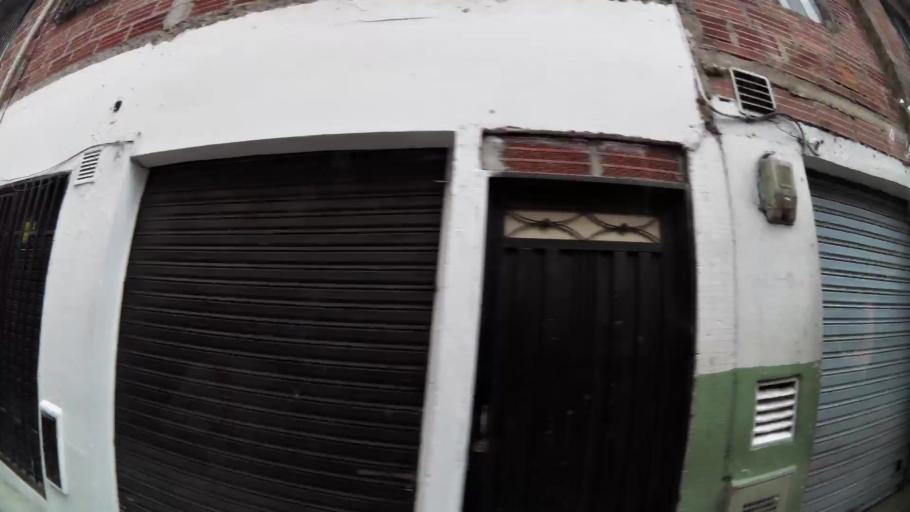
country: CO
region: Antioquia
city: Medellin
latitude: 6.2307
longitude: -75.5550
